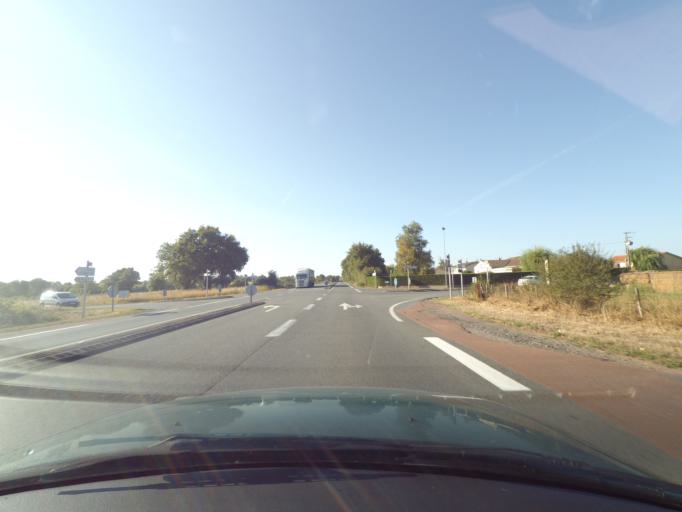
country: FR
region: Poitou-Charentes
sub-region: Departement des Deux-Sevres
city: Chiche
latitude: 46.7457
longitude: -0.3053
